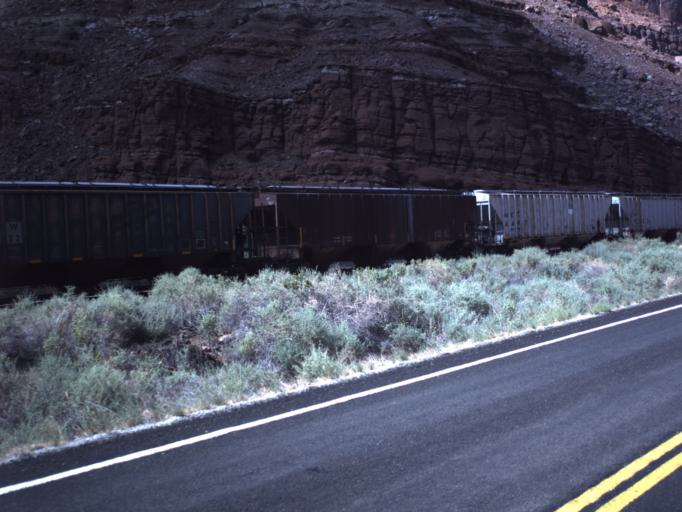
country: US
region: Utah
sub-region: Grand County
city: Moab
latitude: 38.5334
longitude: -109.6564
